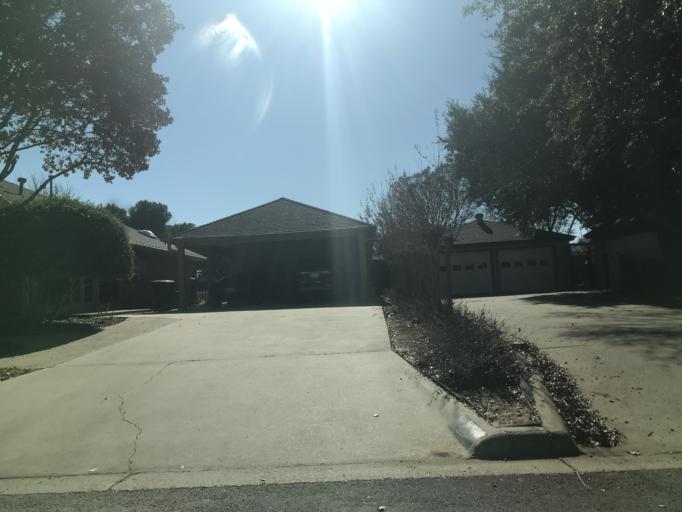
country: US
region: Texas
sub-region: Taylor County
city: Abilene
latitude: 32.3810
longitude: -99.7584
